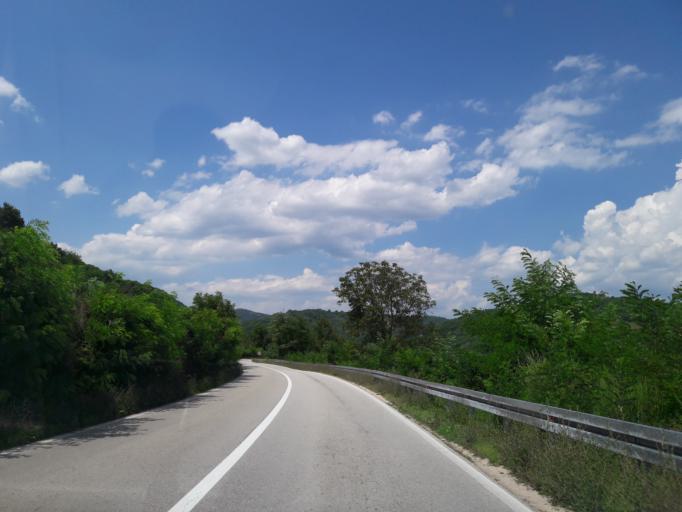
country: BA
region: Republika Srpska
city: Mrkonjic Grad
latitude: 44.5314
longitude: 17.1506
